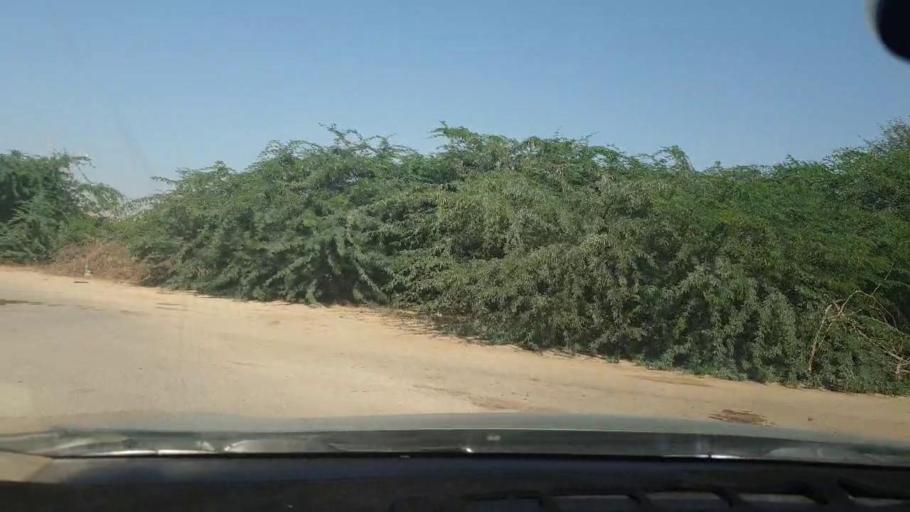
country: PK
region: Sindh
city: Malir Cantonment
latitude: 25.1583
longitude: 67.1652
